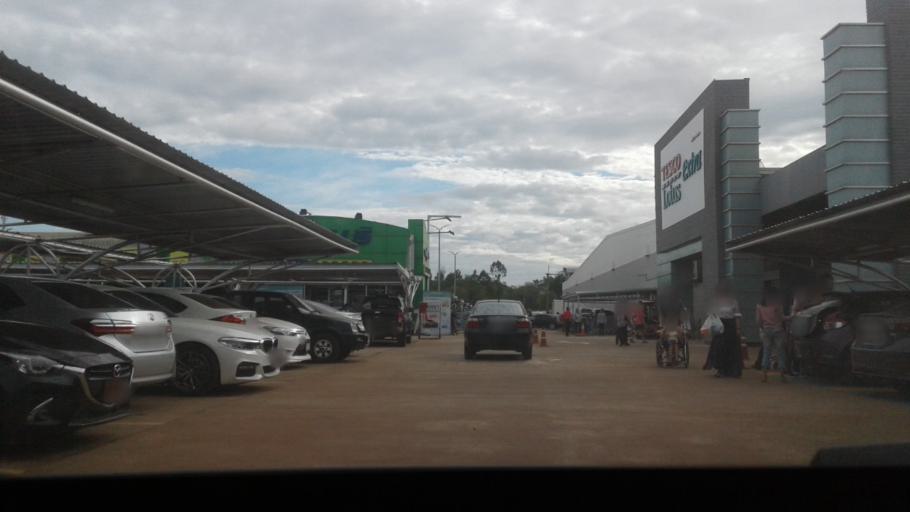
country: TH
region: Changwat Udon Thani
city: Udon Thani
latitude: 17.4316
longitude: 102.7876
